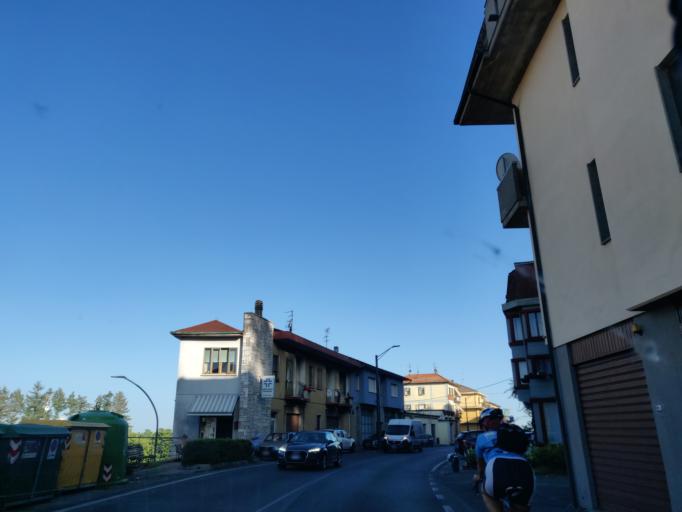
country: IT
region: Tuscany
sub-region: Provincia di Siena
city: Abbadia San Salvatore
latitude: 42.8770
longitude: 11.6824
